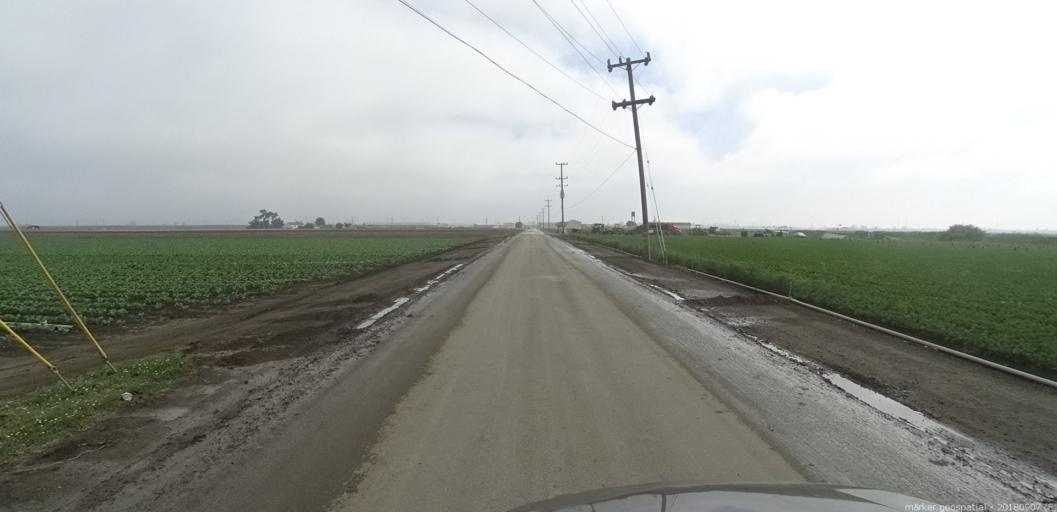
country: US
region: California
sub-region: Monterey County
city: Boronda
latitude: 36.6924
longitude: -121.7066
